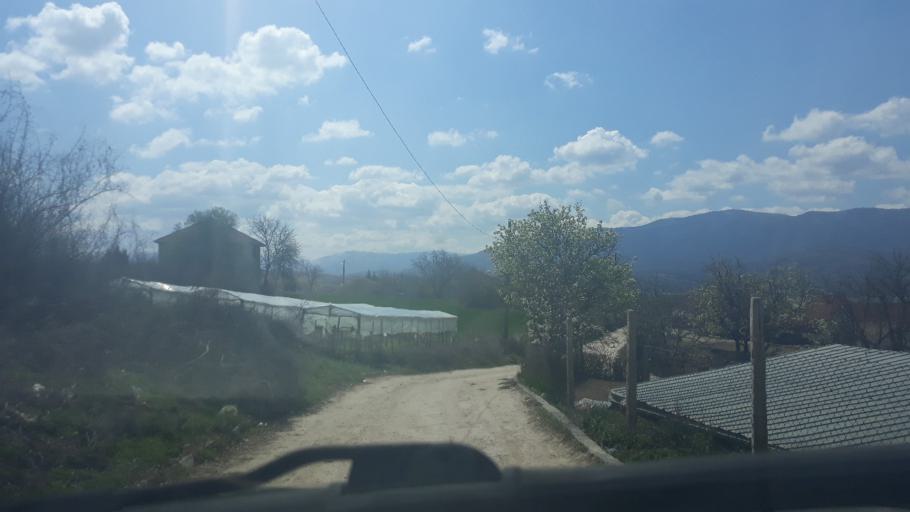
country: MK
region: Caska
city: Caska
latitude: 41.6493
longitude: 21.6956
